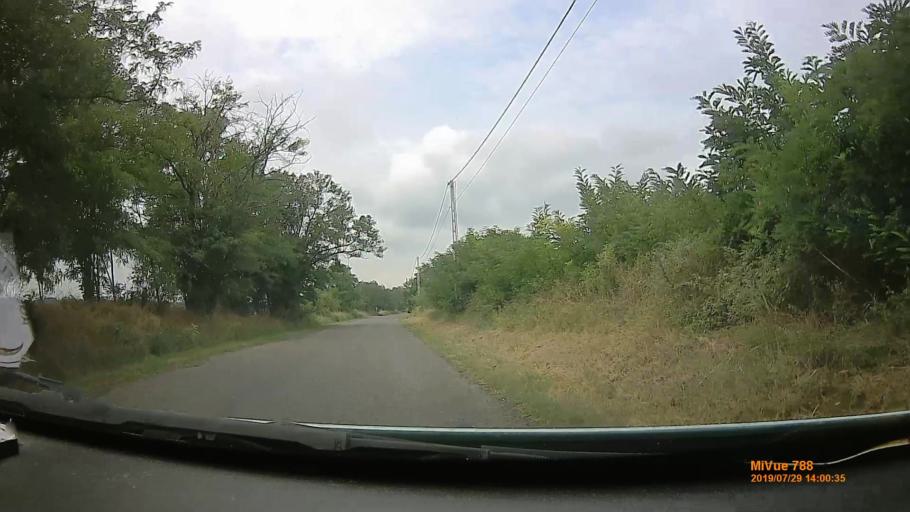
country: HU
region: Somogy
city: Balatonfoldvar
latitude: 46.7901
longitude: 17.9423
